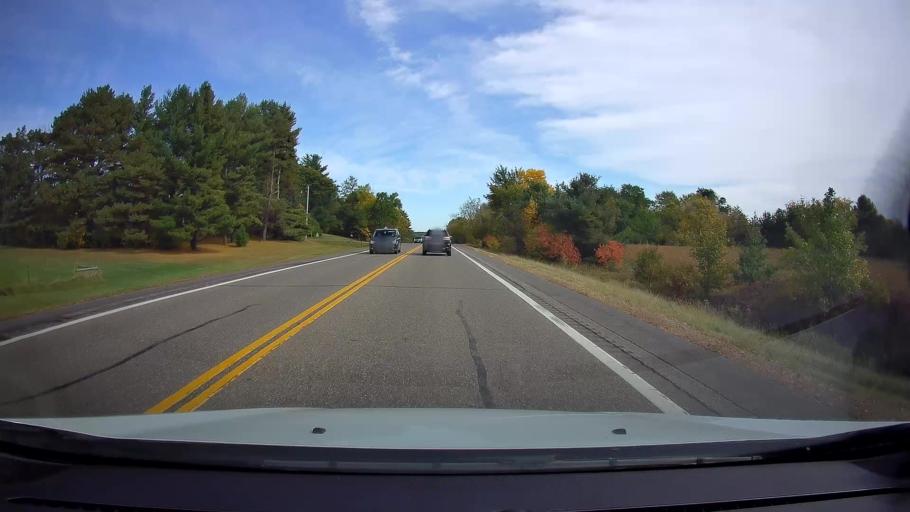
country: US
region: Minnesota
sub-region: Washington County
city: Scandia
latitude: 45.2791
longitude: -92.7771
